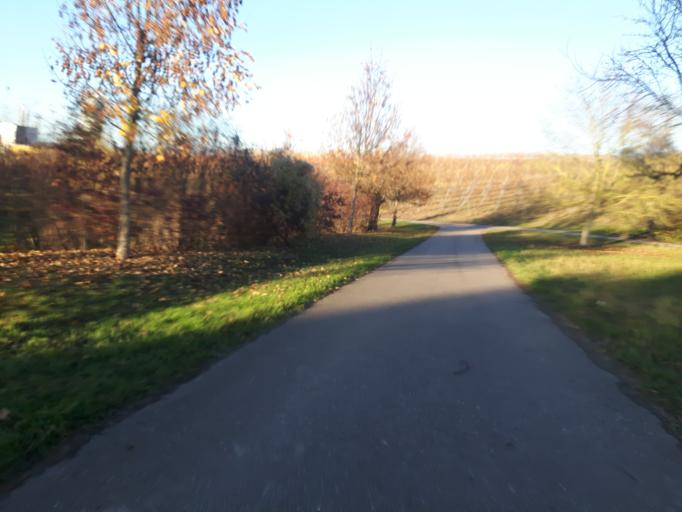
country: DE
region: Baden-Wuerttemberg
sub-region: Regierungsbezirk Stuttgart
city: Neckarsulm
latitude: 49.1758
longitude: 9.2341
